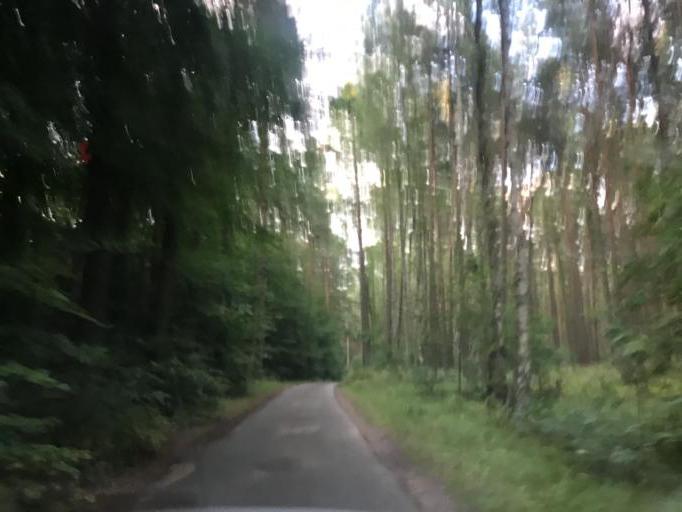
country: DE
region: Mecklenburg-Vorpommern
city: Rechlin
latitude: 53.3522
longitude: 12.8410
